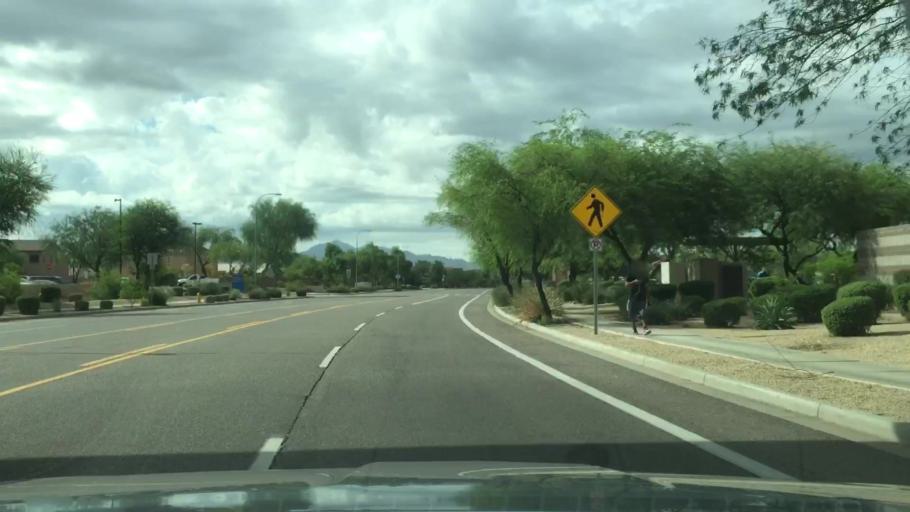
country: US
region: Arizona
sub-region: Maricopa County
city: Tolleson
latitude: 33.4783
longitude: -112.2596
